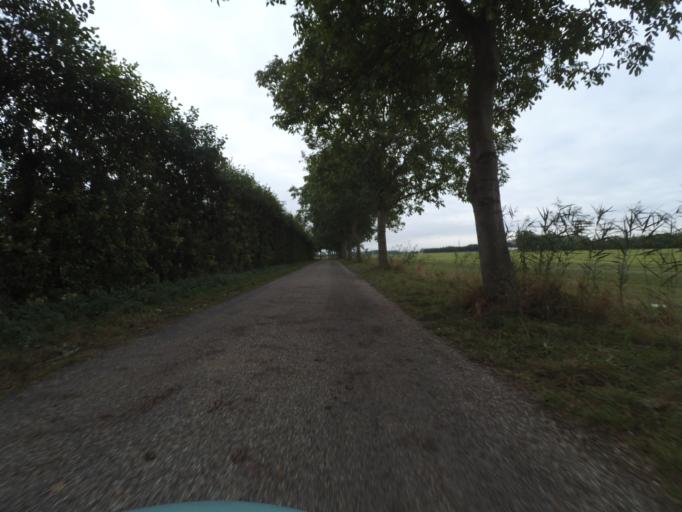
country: NL
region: Utrecht
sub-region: Gemeente Wijk bij Duurstede
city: Wijk bij Duurstede
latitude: 51.9403
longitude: 5.2989
